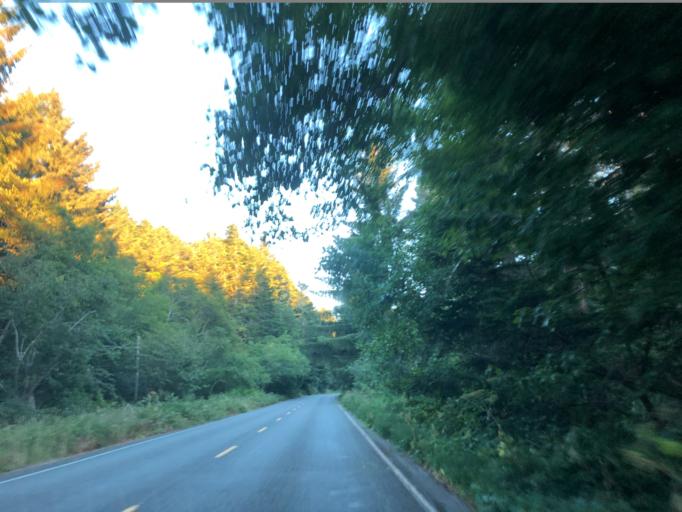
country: US
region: California
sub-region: Humboldt County
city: Westhaven-Moonstone
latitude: 41.0924
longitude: -124.1537
